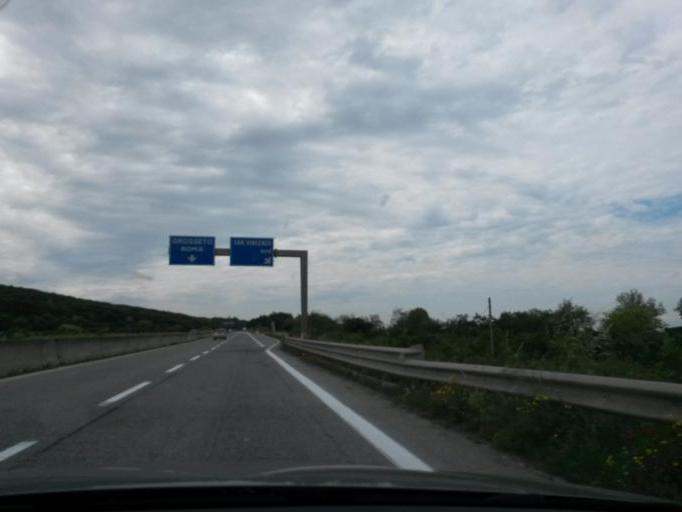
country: IT
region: Tuscany
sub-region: Provincia di Livorno
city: San Vincenzo
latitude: 43.1169
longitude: 10.5446
